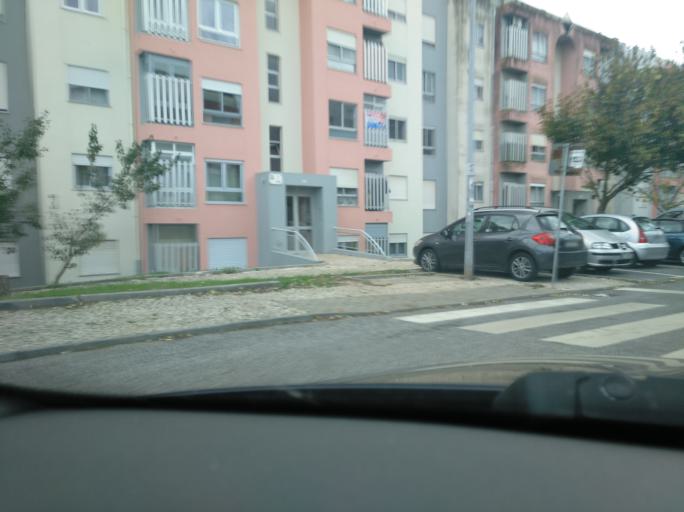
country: PT
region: Lisbon
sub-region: Amadora
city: Amadora
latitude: 38.7363
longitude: -9.2095
